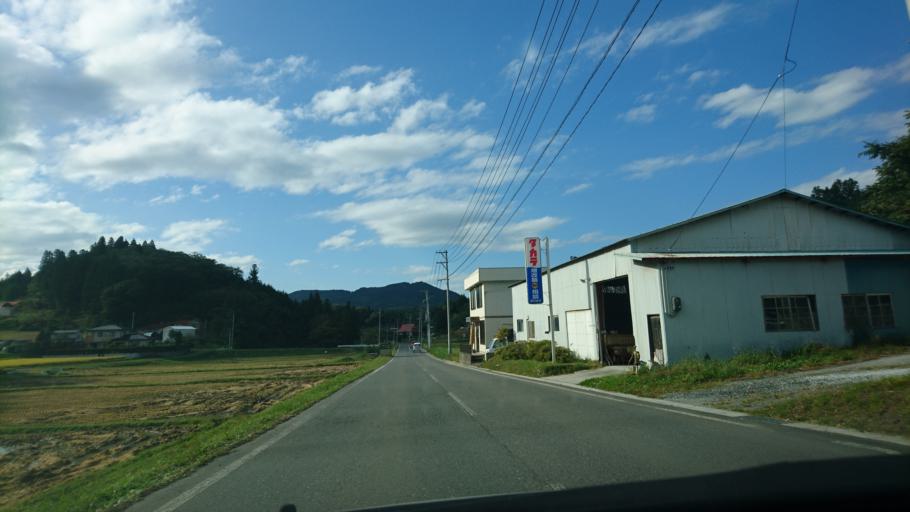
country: JP
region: Iwate
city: Ichinoseki
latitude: 38.8945
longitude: 141.3291
